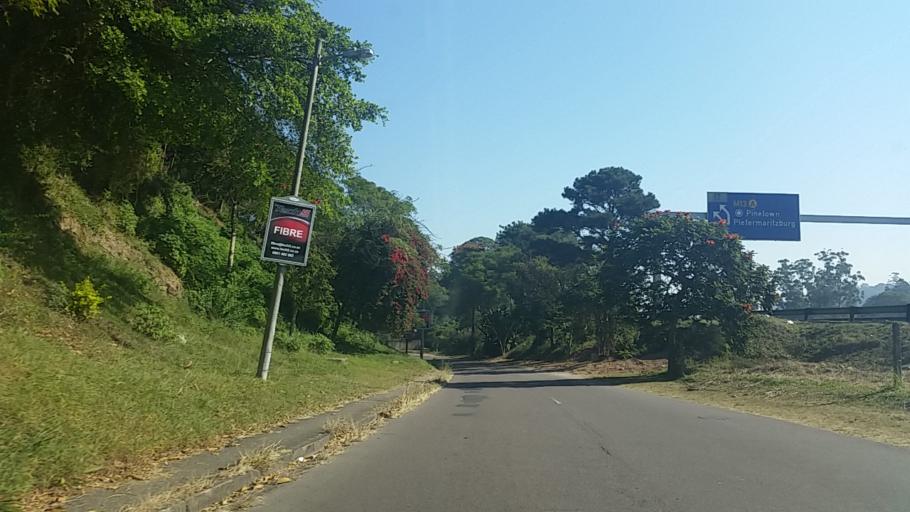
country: ZA
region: KwaZulu-Natal
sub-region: eThekwini Metropolitan Municipality
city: Berea
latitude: -29.8370
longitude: 30.9040
